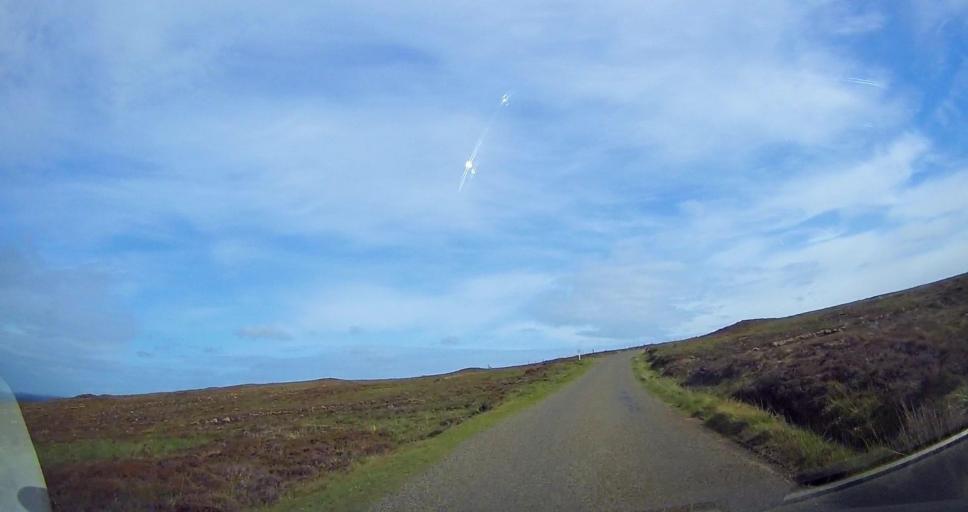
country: GB
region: Scotland
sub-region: Orkney Islands
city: Stromness
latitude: 58.8673
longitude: -3.2211
